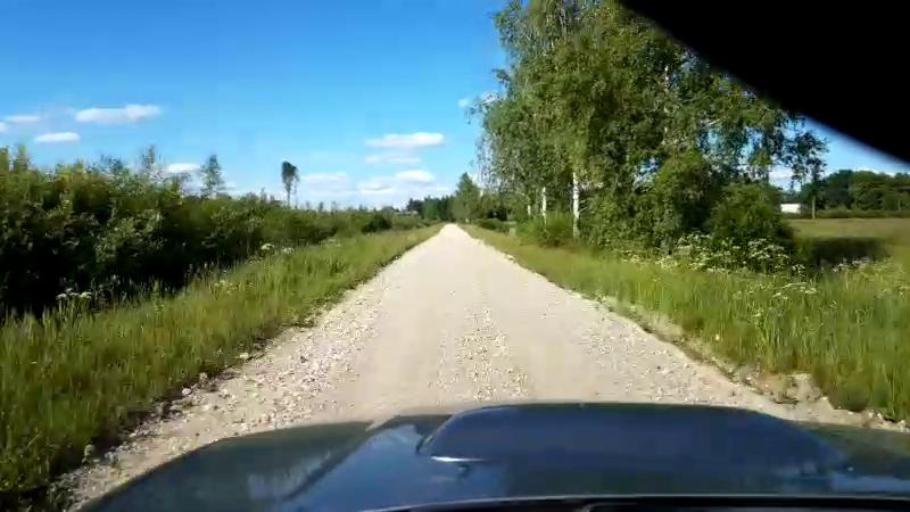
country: EE
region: Paernumaa
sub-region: Sauga vald
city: Sauga
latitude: 58.5018
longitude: 24.5644
